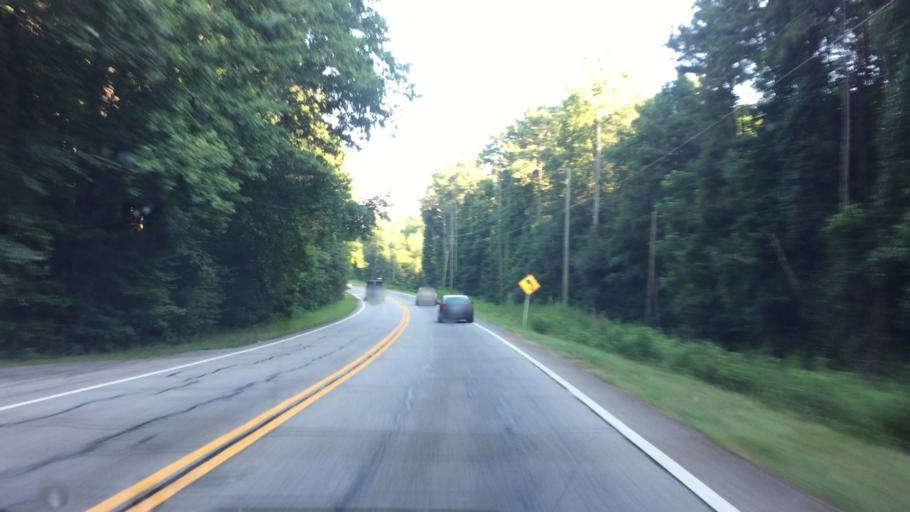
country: US
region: Georgia
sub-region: DeKalb County
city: Pine Mountain
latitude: 33.6294
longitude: -84.1818
